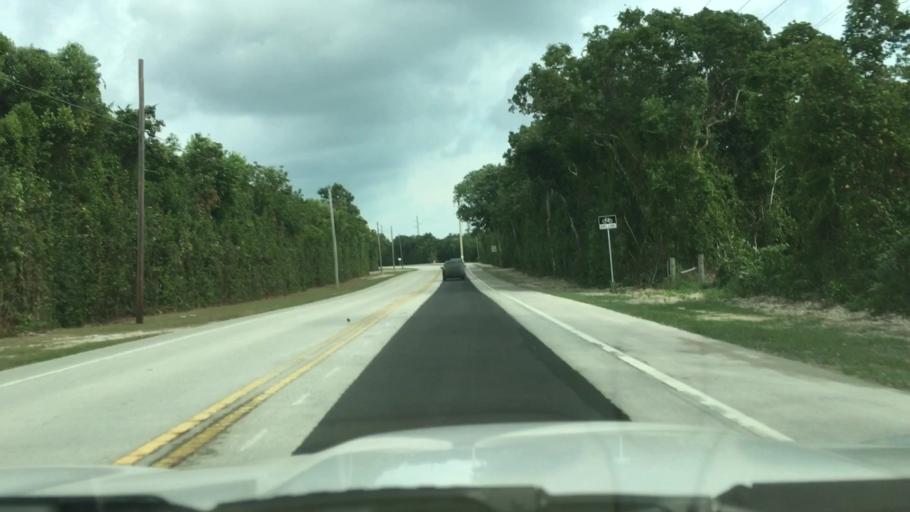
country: US
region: Florida
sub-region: Monroe County
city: North Key Largo
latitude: 25.2261
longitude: -80.3305
